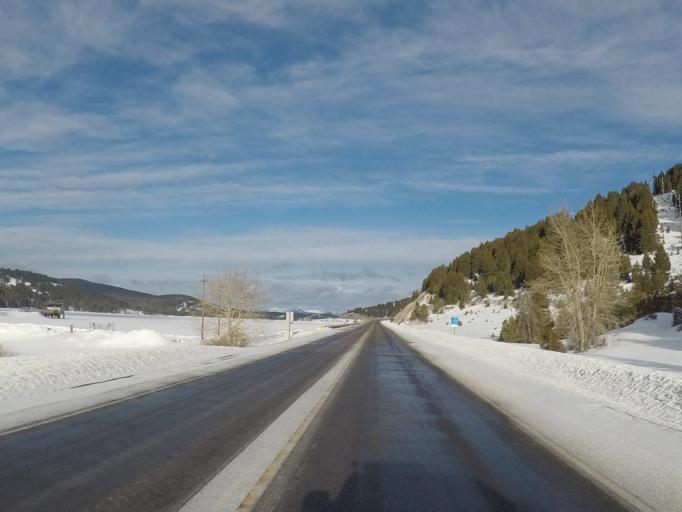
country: US
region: Montana
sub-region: Granite County
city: Philipsburg
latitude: 46.1673
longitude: -113.2148
